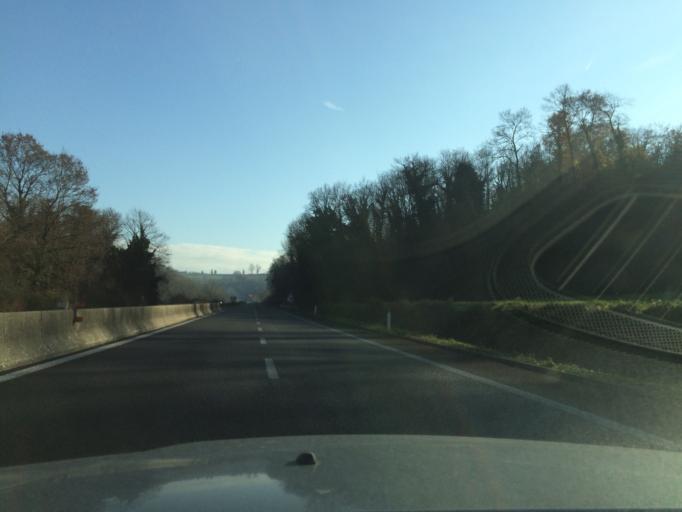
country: IT
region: Umbria
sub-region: Provincia di Perugia
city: Todi
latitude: 42.7540
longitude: 12.4630
